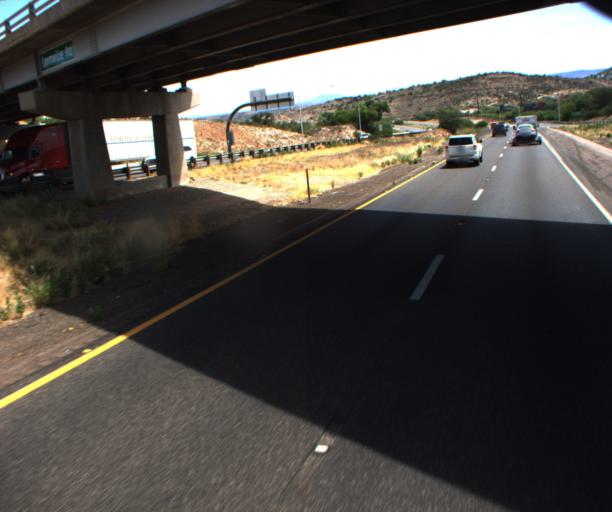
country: US
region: Arizona
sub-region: Yavapai County
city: Lake Montezuma
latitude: 34.6386
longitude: -111.8174
